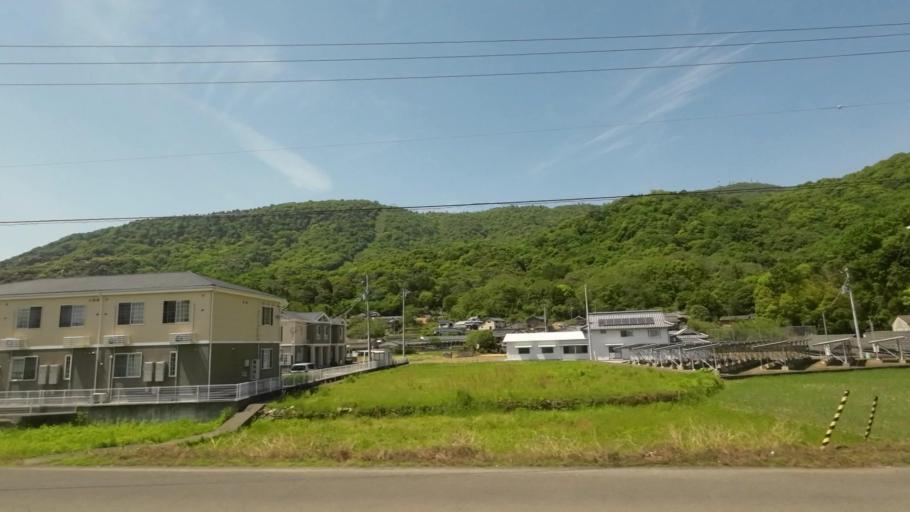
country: JP
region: Kagawa
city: Marugame
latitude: 34.2001
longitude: 133.8100
